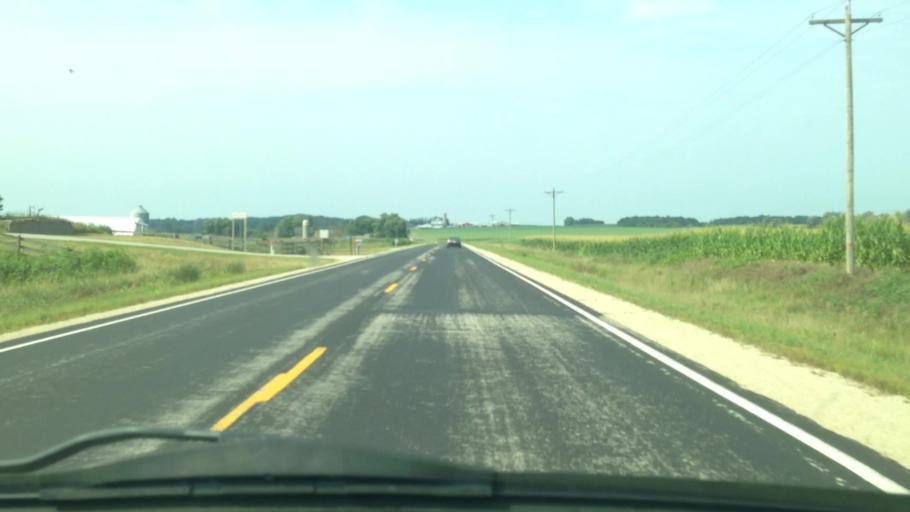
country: US
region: Minnesota
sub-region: Winona County
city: Lewiston
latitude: 43.9445
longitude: -91.9550
